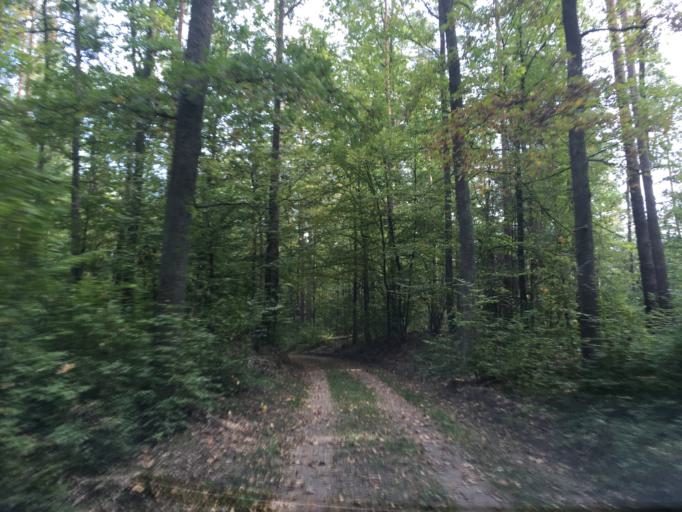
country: PL
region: Kujawsko-Pomorskie
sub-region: Powiat brodnicki
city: Gorzno
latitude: 53.2218
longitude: 19.7053
